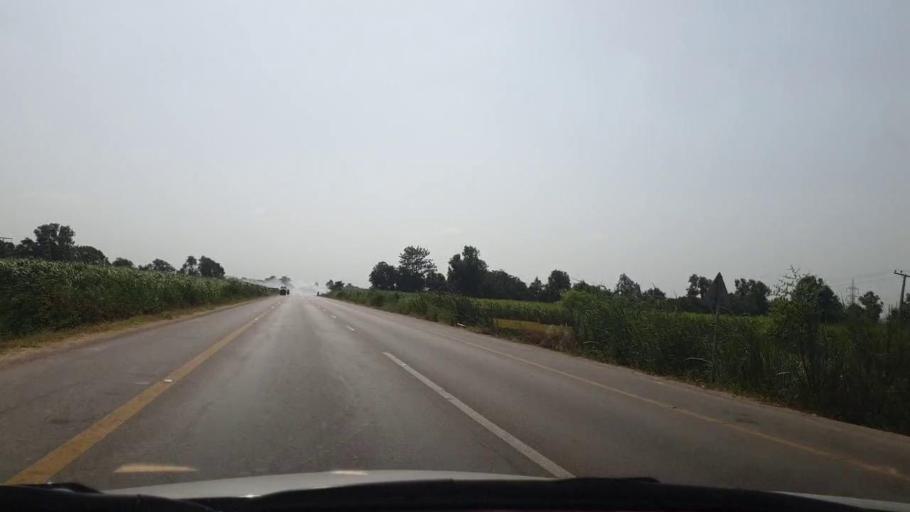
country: PK
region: Sindh
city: Matli
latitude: 25.0778
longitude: 68.6143
